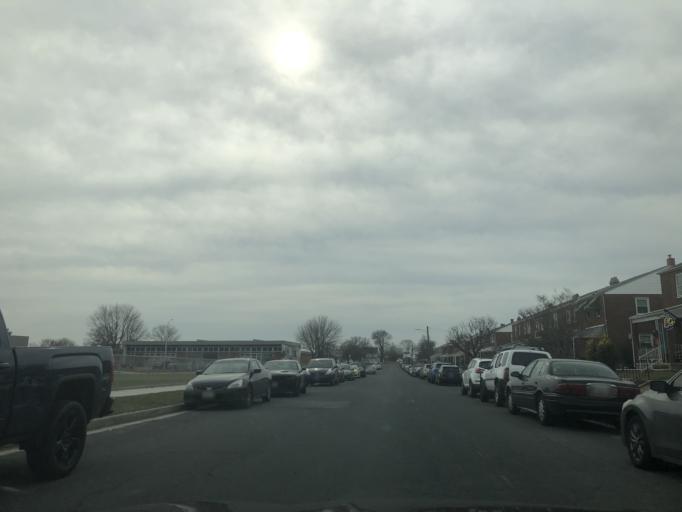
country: US
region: Maryland
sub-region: Baltimore County
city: Dundalk
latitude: 39.2674
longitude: -76.4894
